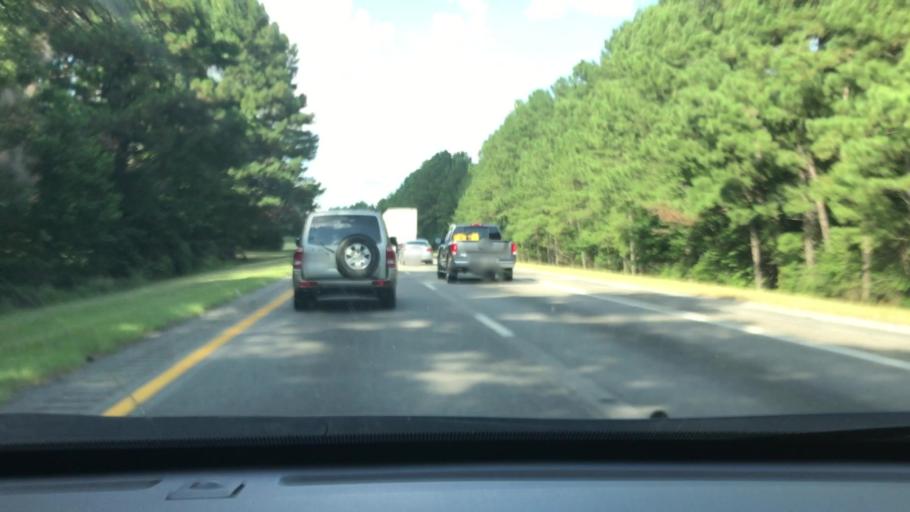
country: US
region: South Carolina
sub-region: Florence County
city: Timmonsville
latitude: 33.9926
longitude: -80.0150
